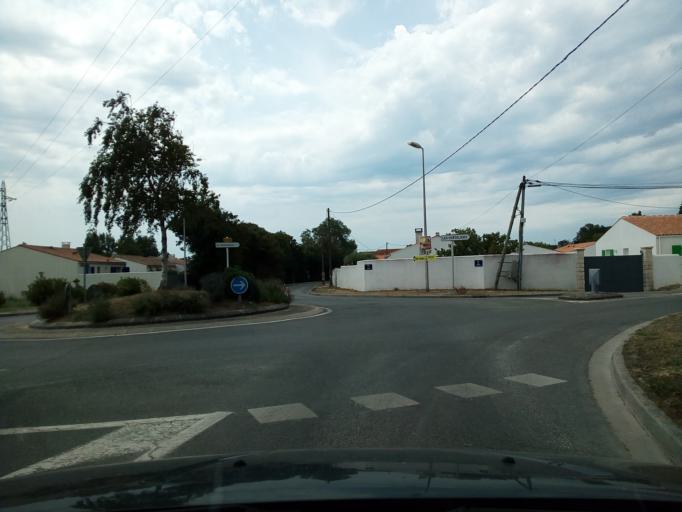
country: FR
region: Poitou-Charentes
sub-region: Departement de la Charente-Maritime
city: Dolus-d'Oleron
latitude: 45.9276
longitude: -1.3190
